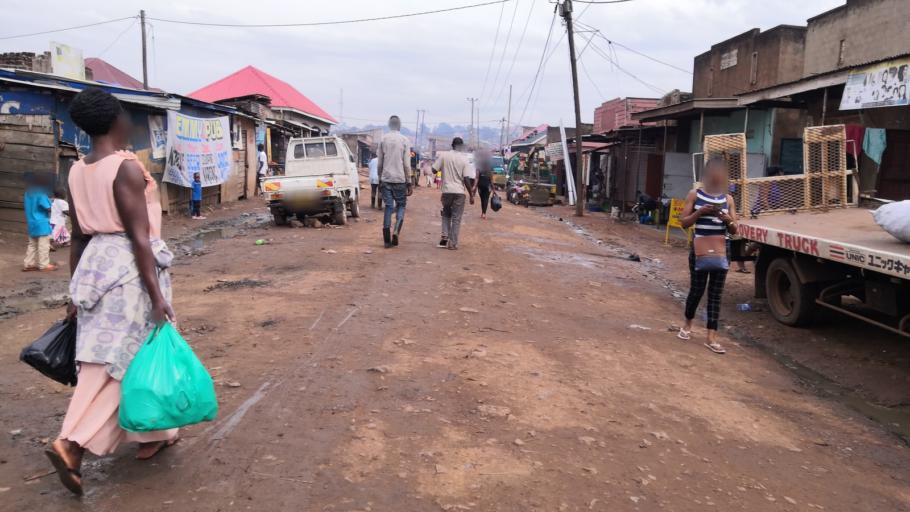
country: UG
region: Central Region
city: Kampala Central Division
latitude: 0.3508
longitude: 32.5703
